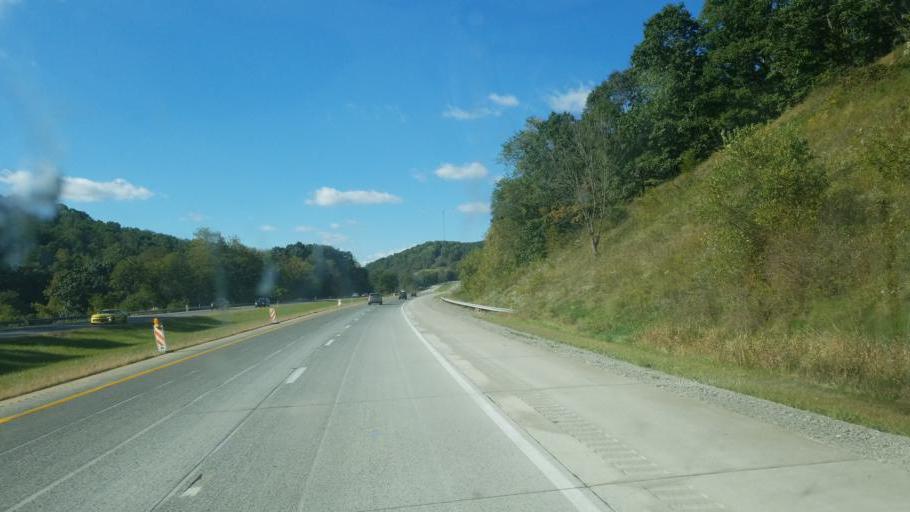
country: US
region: West Virginia
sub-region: Monongalia County
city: Star City
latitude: 39.7508
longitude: -80.0756
